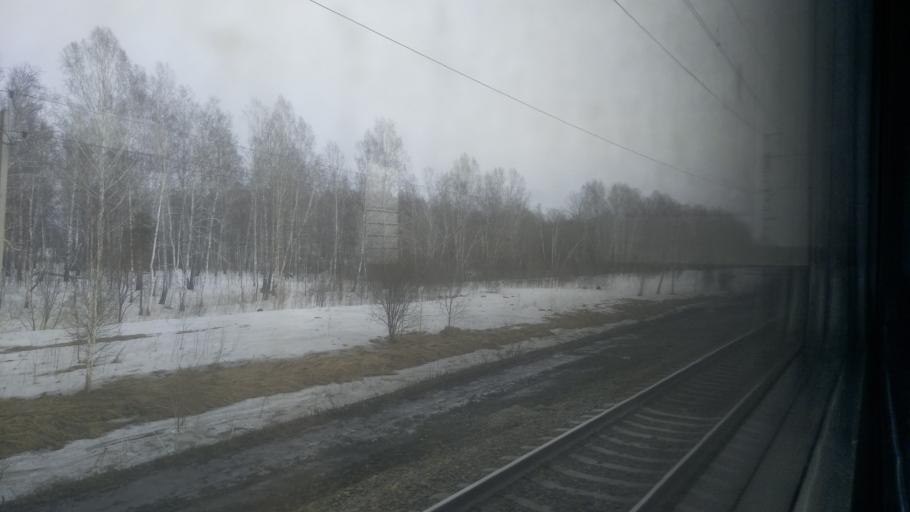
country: RU
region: Novosibirsk
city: Stantsionno-Oyashinskiy
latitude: 55.5058
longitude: 83.9228
